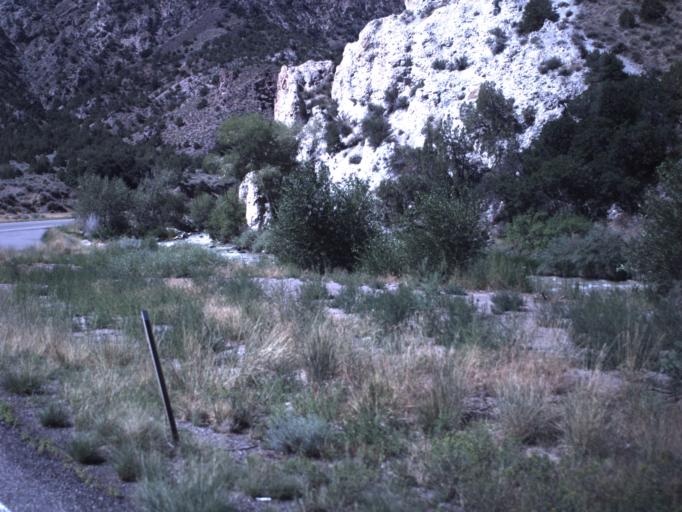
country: US
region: Utah
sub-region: Sevier County
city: Monroe
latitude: 38.5694
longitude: -112.2526
